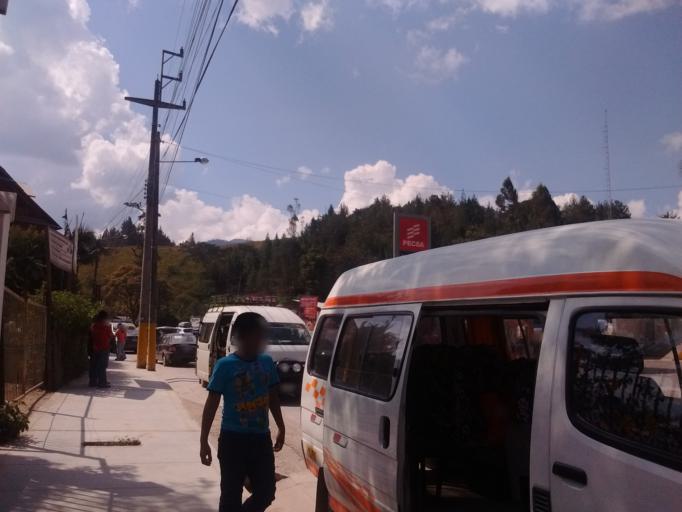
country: PE
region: Pasco
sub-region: Provincia de Oxapampa
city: Oxapampa
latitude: -10.5697
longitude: -75.4074
